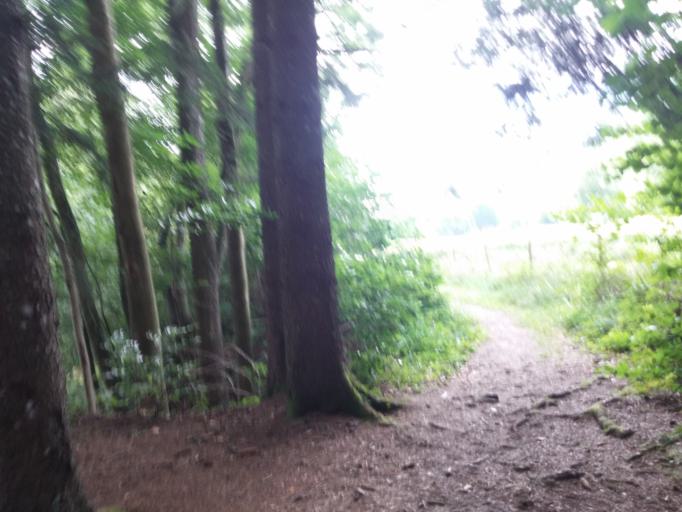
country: DE
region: Bavaria
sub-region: Swabia
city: Kronburg
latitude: 47.8712
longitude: 10.1897
